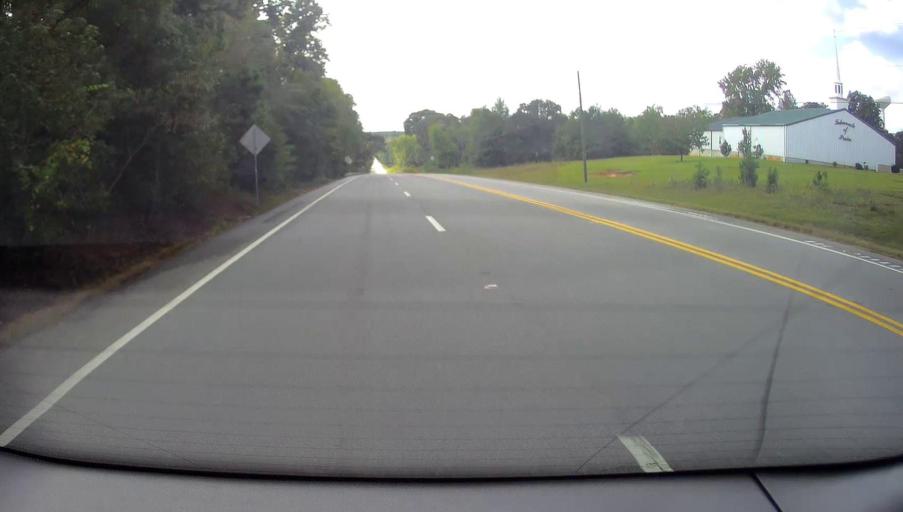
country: US
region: Georgia
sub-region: Baldwin County
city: Milledgeville
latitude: 33.0593
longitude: -83.2775
